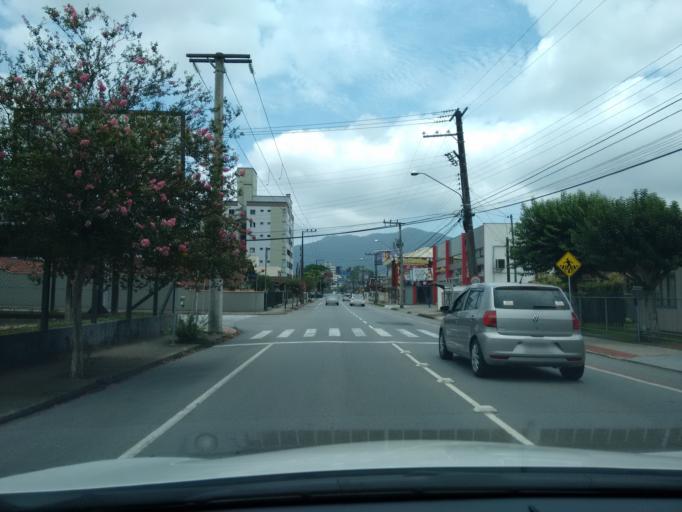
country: BR
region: Santa Catarina
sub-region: Jaragua Do Sul
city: Jaragua do Sul
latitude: -26.4995
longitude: -49.0809
